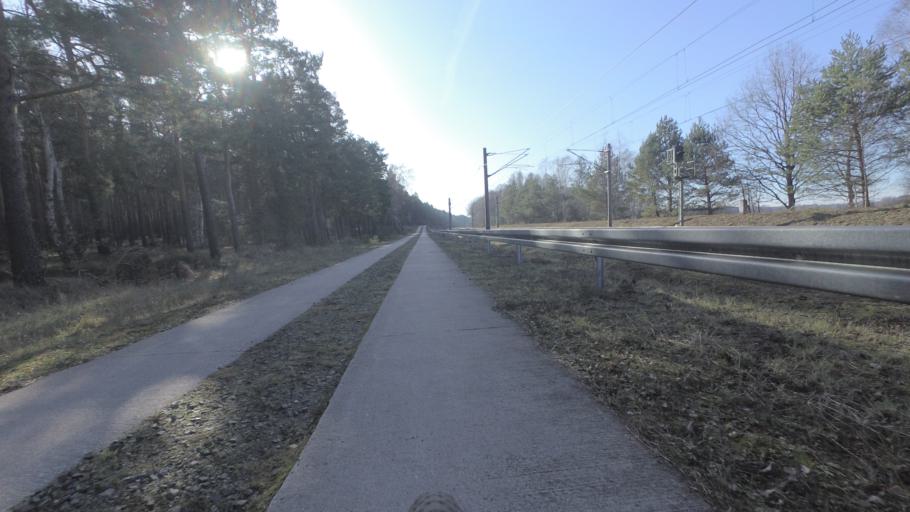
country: DE
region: Brandenburg
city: Luckenwalde
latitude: 52.1419
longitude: 13.2190
